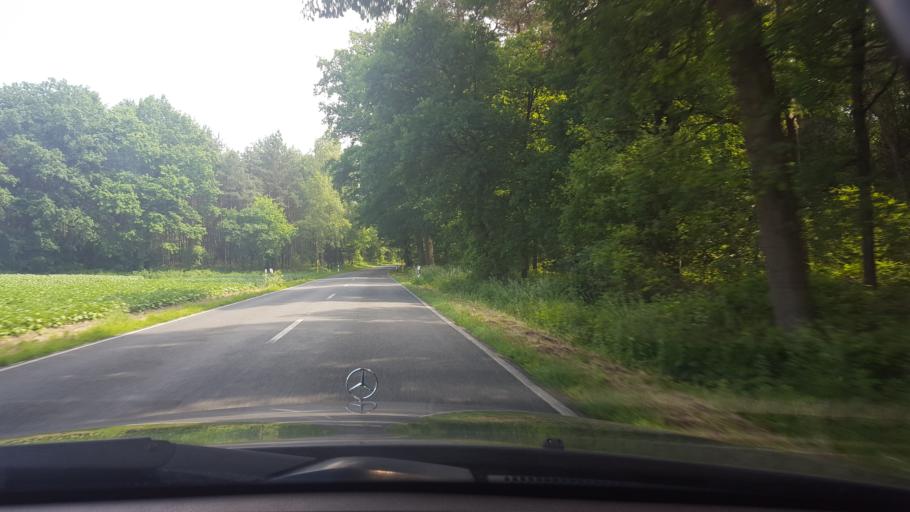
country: DE
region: North Rhine-Westphalia
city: Olfen
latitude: 51.7206
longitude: 7.3041
